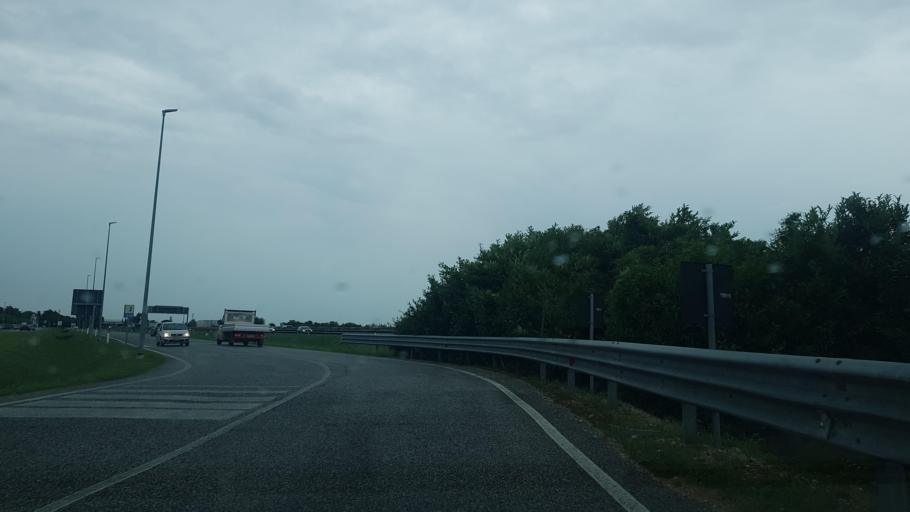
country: IT
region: Friuli Venezia Giulia
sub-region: Provincia di Udine
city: Visco
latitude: 45.8856
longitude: 13.3389
